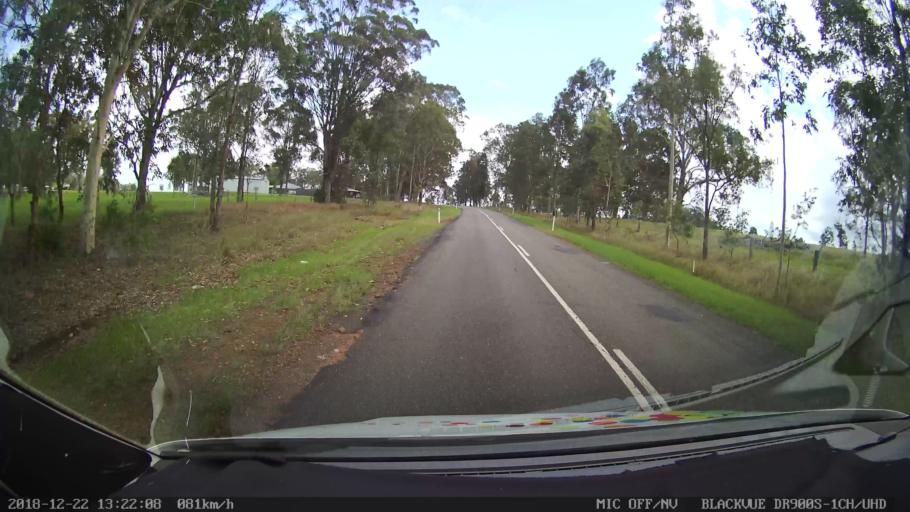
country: AU
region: New South Wales
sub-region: Clarence Valley
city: Coutts Crossing
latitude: -29.7838
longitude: 152.9139
